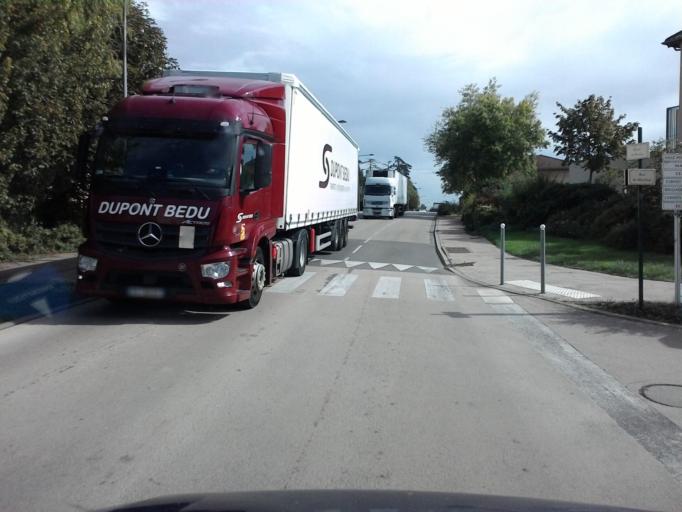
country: FR
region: Rhone-Alpes
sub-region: Departement de l'Ain
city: Saint-Cyr-sur-Menthon
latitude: 46.2763
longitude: 4.9722
